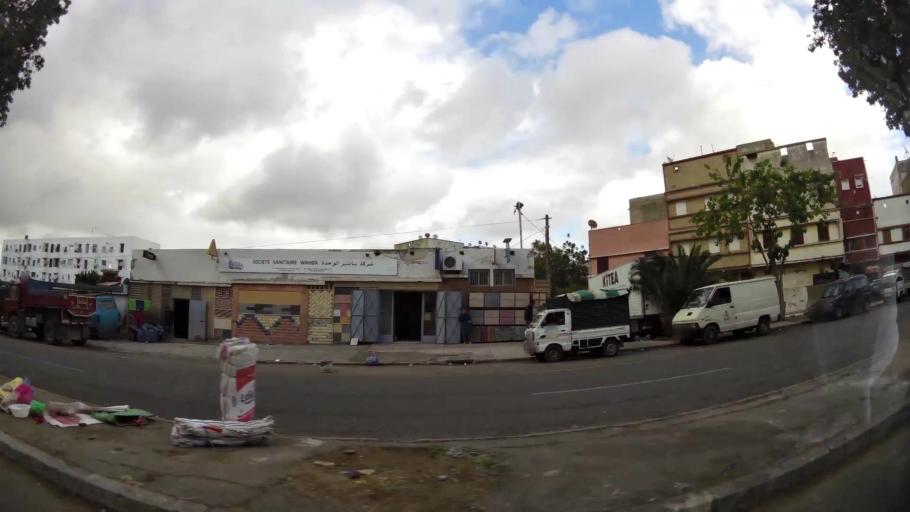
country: MA
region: Grand Casablanca
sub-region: Casablanca
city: Casablanca
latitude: 33.5482
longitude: -7.6009
